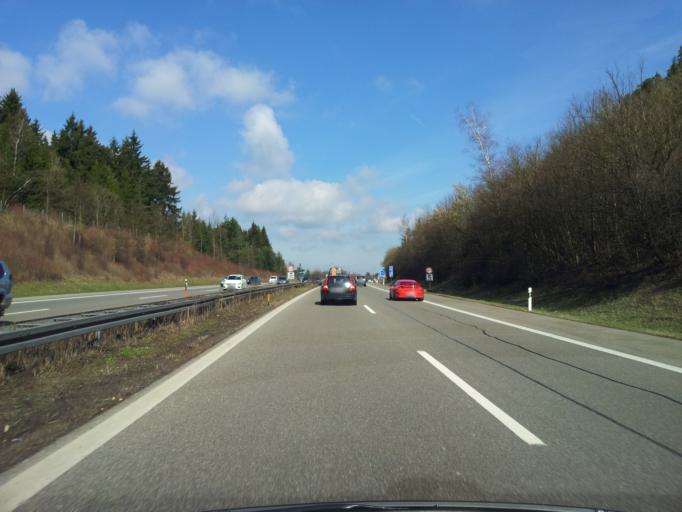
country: DE
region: Baden-Wuerttemberg
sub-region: Freiburg Region
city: Vohringen
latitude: 48.2908
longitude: 8.6373
